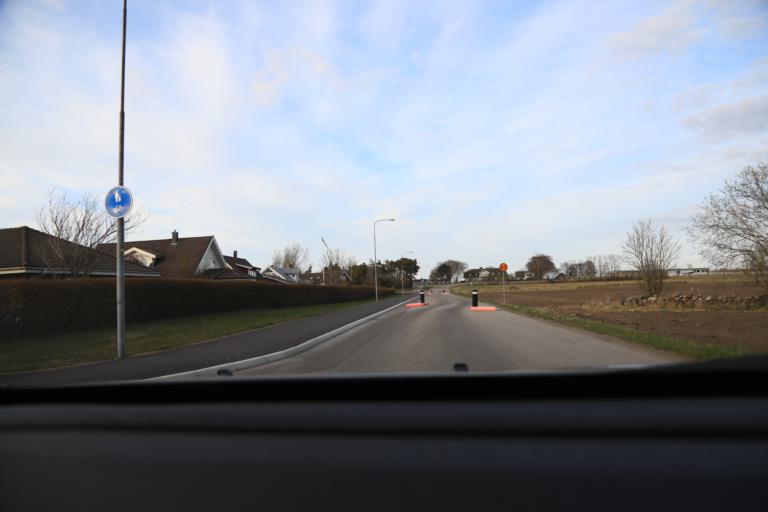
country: SE
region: Halland
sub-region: Varbergs Kommun
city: Traslovslage
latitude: 57.0766
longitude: 12.2767
